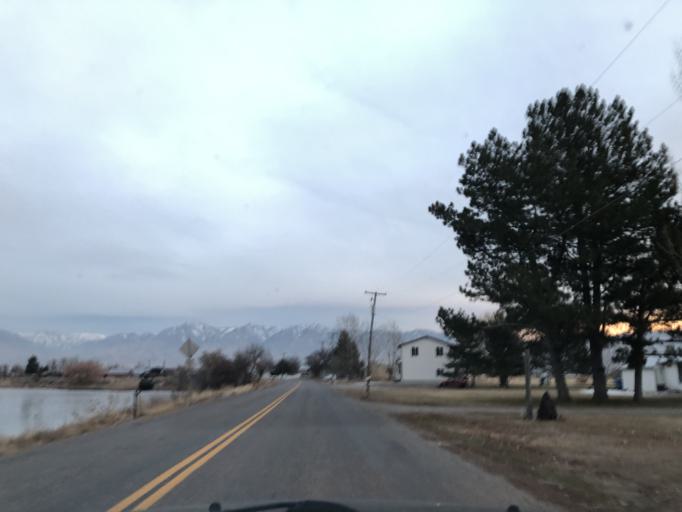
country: US
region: Utah
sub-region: Cache County
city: Benson
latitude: 41.7905
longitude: -111.9107
